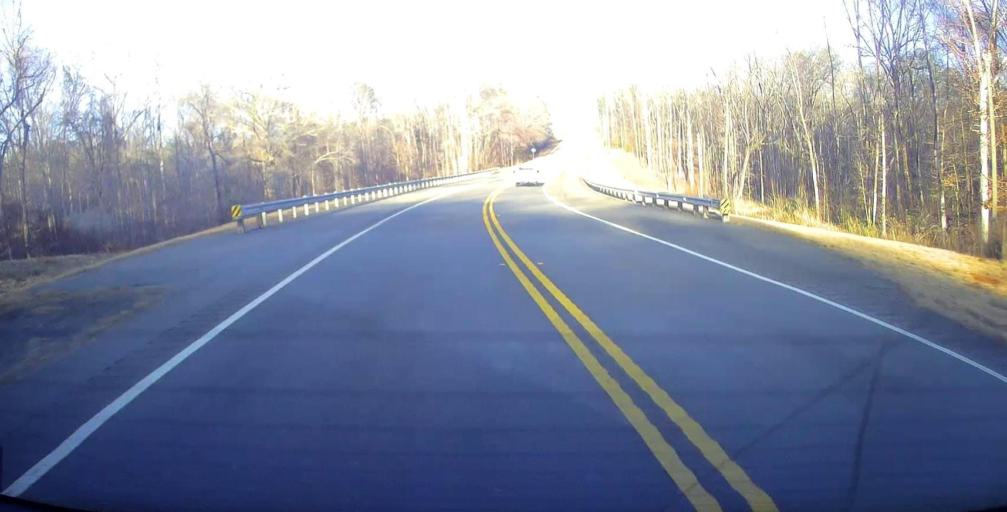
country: US
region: Georgia
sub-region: Upson County
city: Thomaston
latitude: 32.8419
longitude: -84.4229
